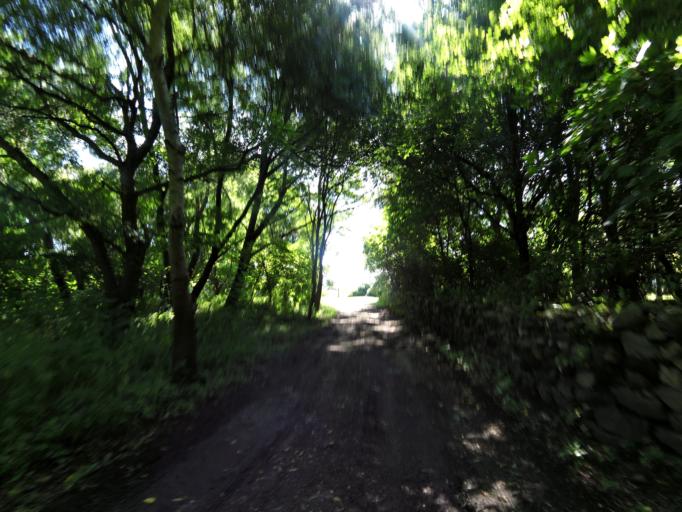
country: HU
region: Veszprem
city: Tapolca
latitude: 46.8330
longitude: 17.4028
